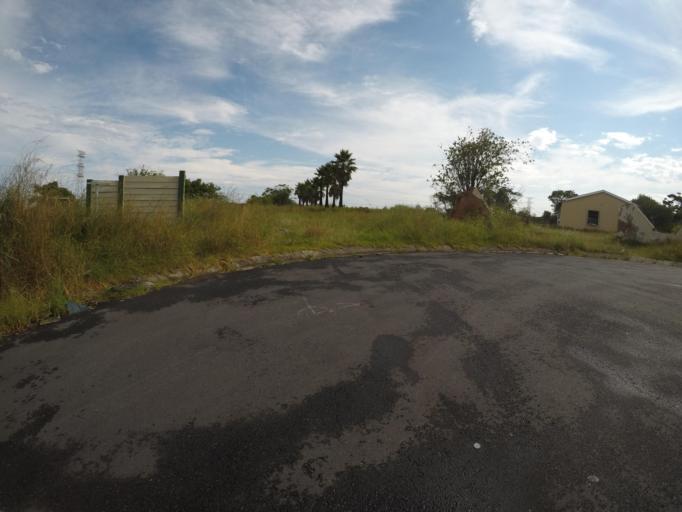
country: ZA
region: Eastern Cape
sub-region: Buffalo City Metropolitan Municipality
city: East London
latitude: -33.0236
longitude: 27.8729
